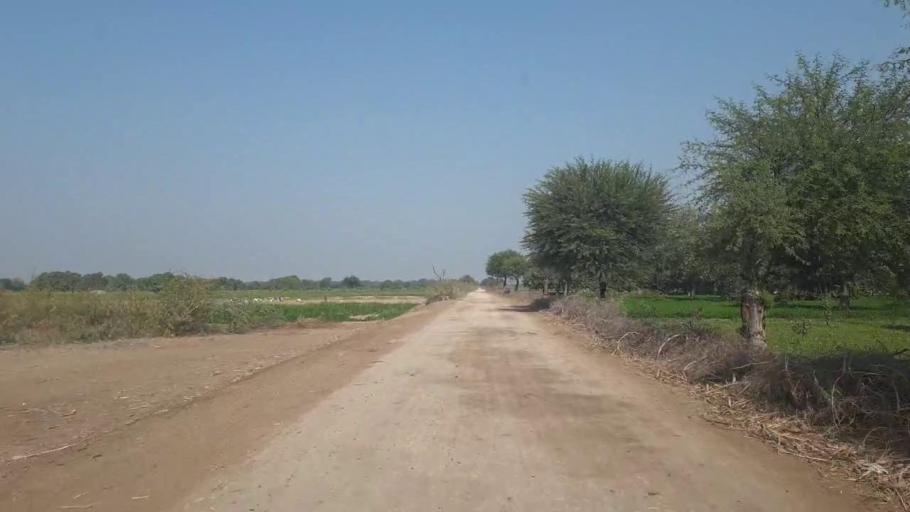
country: PK
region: Sindh
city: Tando Allahyar
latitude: 25.4396
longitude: 68.8499
